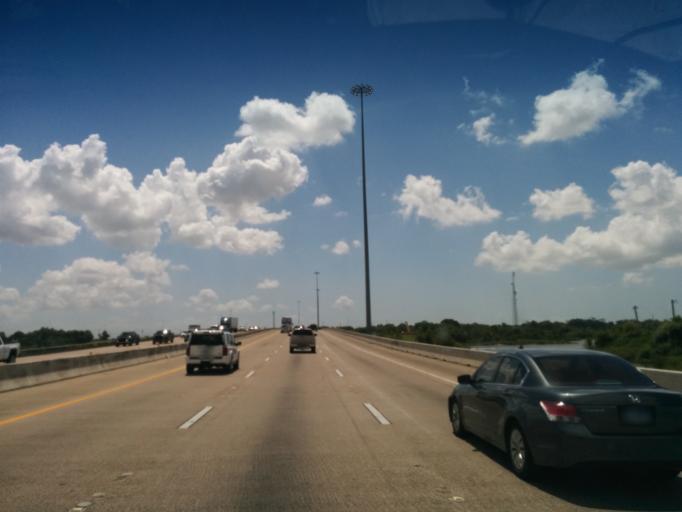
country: US
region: Texas
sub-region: Harris County
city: Highlands
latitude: 29.7938
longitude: -95.0642
